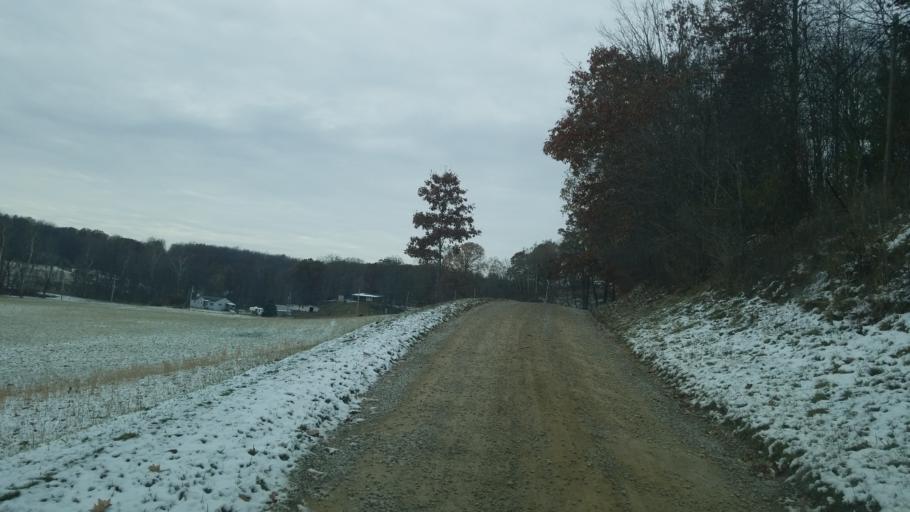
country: US
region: Ohio
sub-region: Licking County
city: Utica
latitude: 40.1733
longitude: -82.3752
